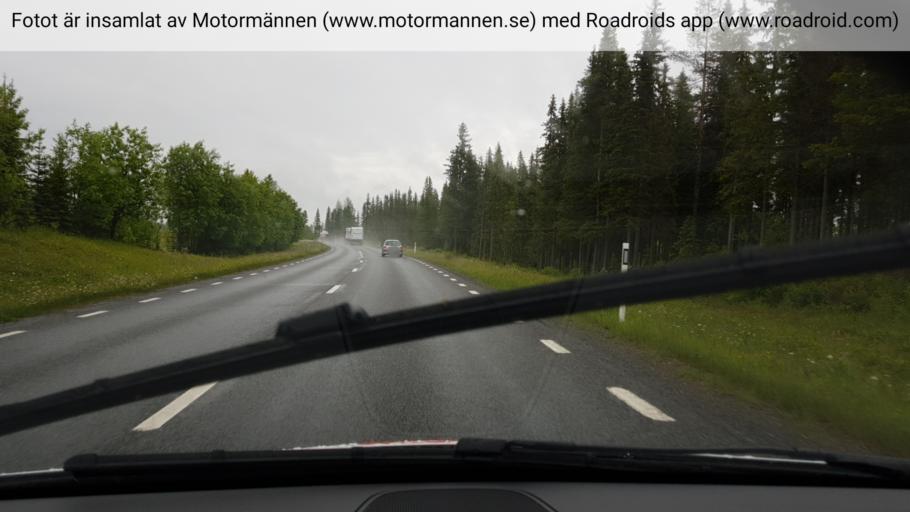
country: SE
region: Jaemtland
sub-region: Stroemsunds Kommun
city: Stroemsund
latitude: 63.5067
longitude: 15.2778
